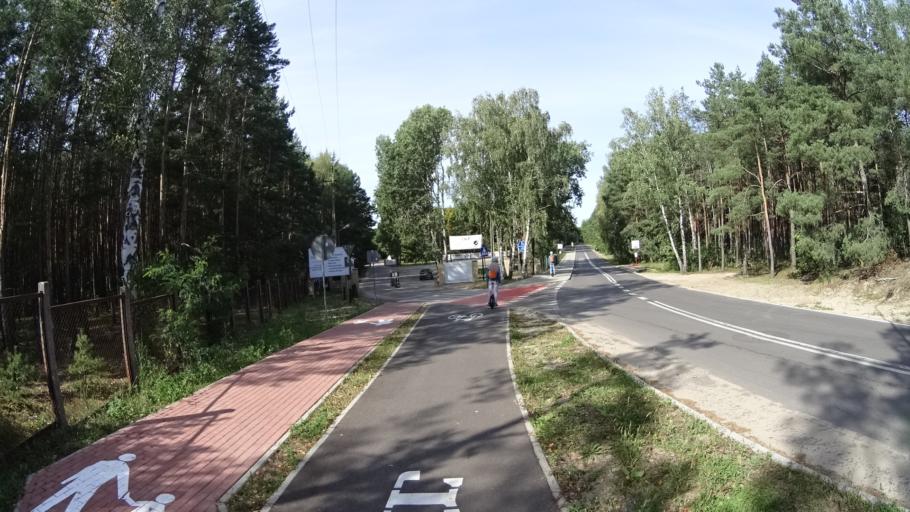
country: PL
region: Masovian Voivodeship
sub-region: Powiat legionowski
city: Bialobrzegi
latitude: 52.4639
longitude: 21.0756
